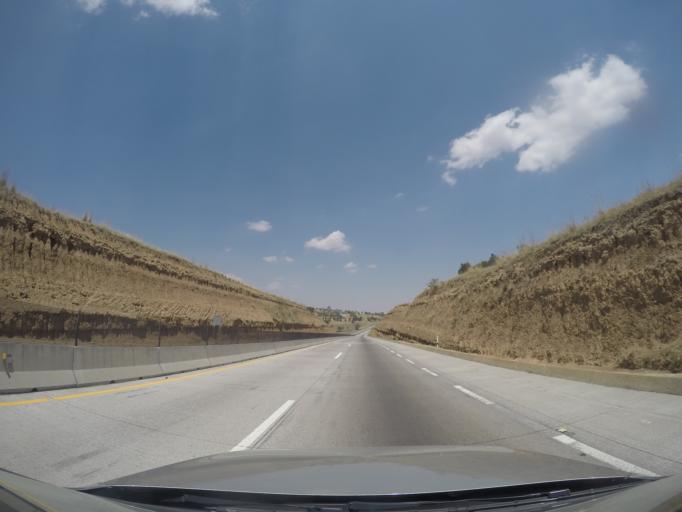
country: MX
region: Tlaxcala
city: Sanctorum
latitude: 19.4854
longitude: -98.4599
